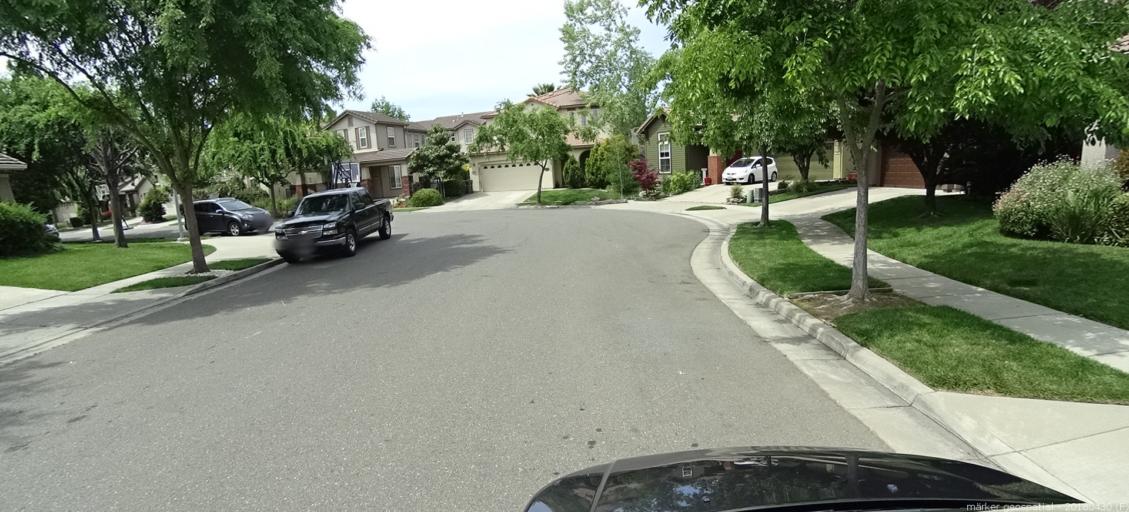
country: US
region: California
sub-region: Yolo County
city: West Sacramento
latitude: 38.5533
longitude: -121.5276
